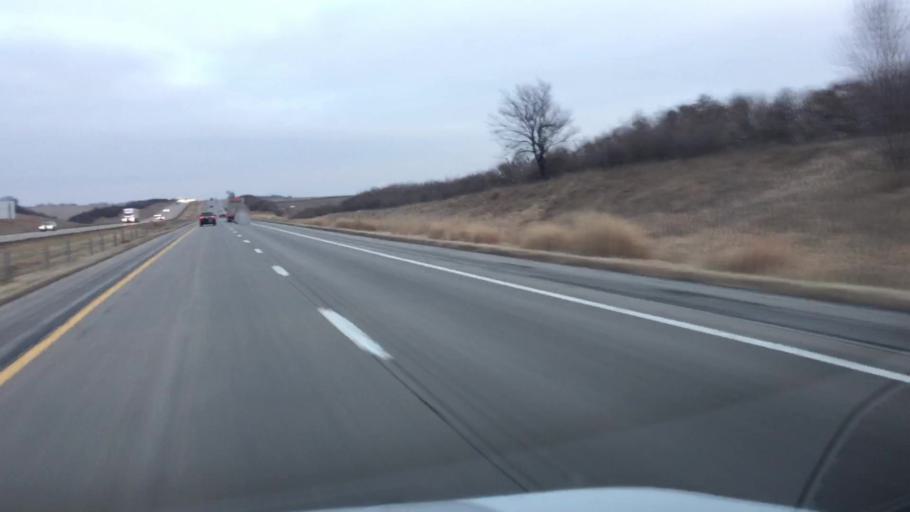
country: US
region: Iowa
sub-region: Jasper County
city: Newton
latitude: 41.6798
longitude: -92.9394
